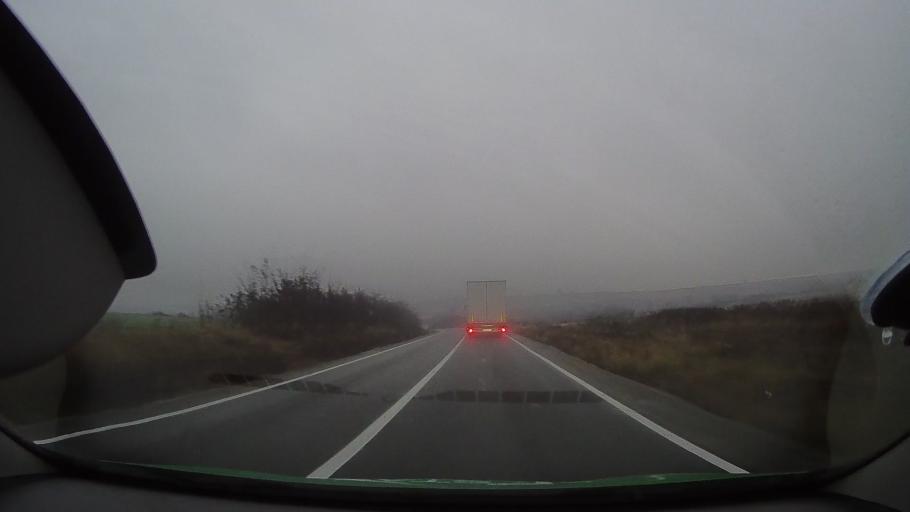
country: RO
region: Bihor
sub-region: Comuna Olcea
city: Calacea
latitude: 46.6506
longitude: 21.9585
